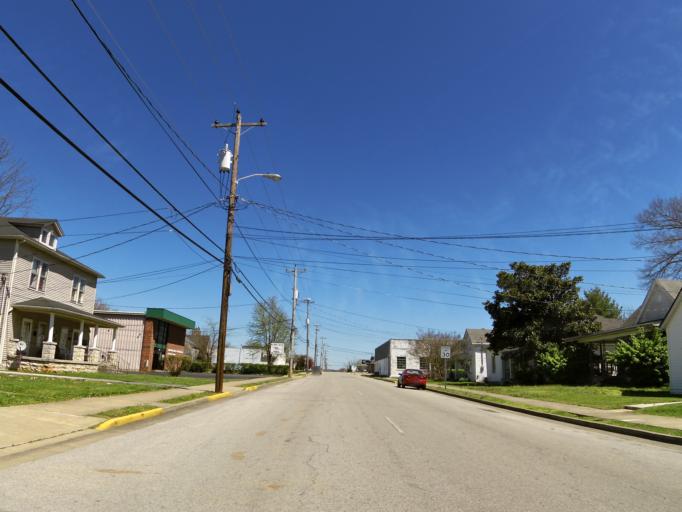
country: US
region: Kentucky
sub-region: Warren County
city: Bowling Green
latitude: 36.9972
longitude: -86.4339
